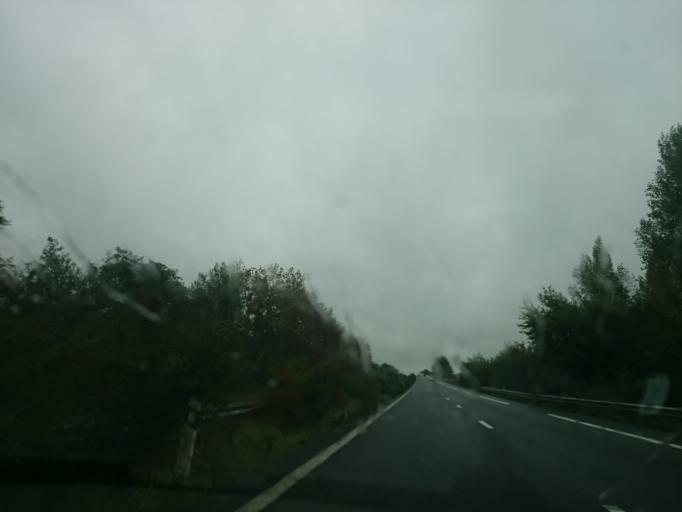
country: FR
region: Pays de la Loire
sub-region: Departement de la Loire-Atlantique
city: Missillac
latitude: 47.4632
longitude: -2.1522
